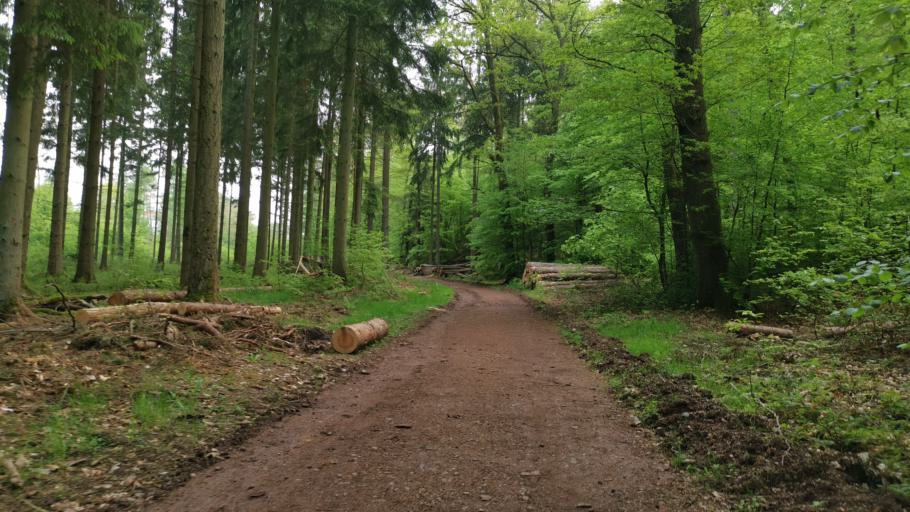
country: DE
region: Saarland
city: Sankt Ingbert
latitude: 49.2598
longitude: 7.1712
